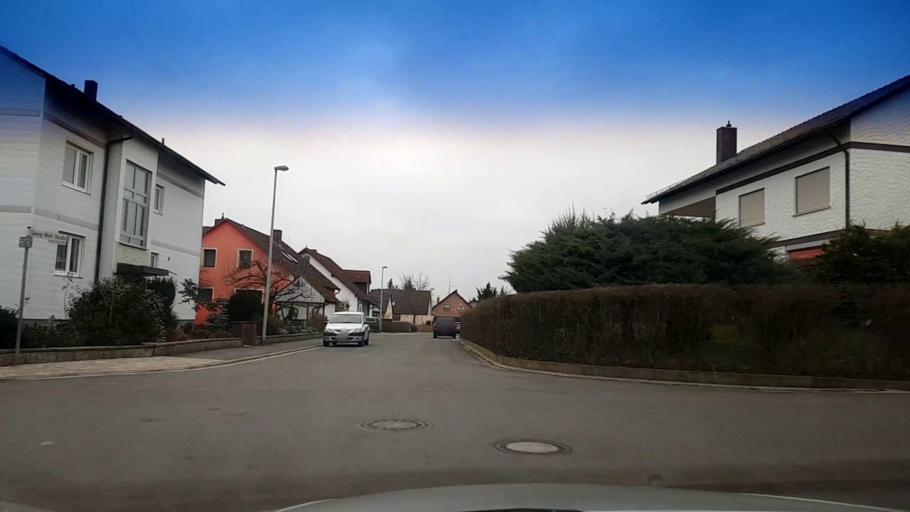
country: DE
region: Bavaria
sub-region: Upper Franconia
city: Gundelsheim
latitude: 49.9389
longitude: 10.9239
